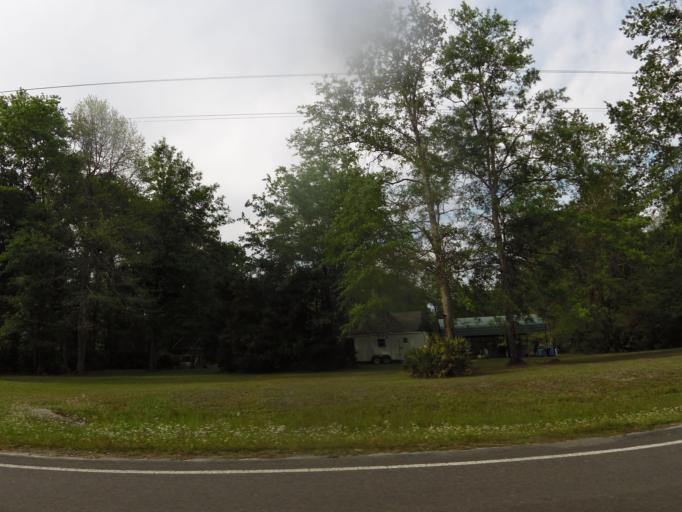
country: US
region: Georgia
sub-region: Camden County
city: Kingsland
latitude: 30.7000
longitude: -81.7507
